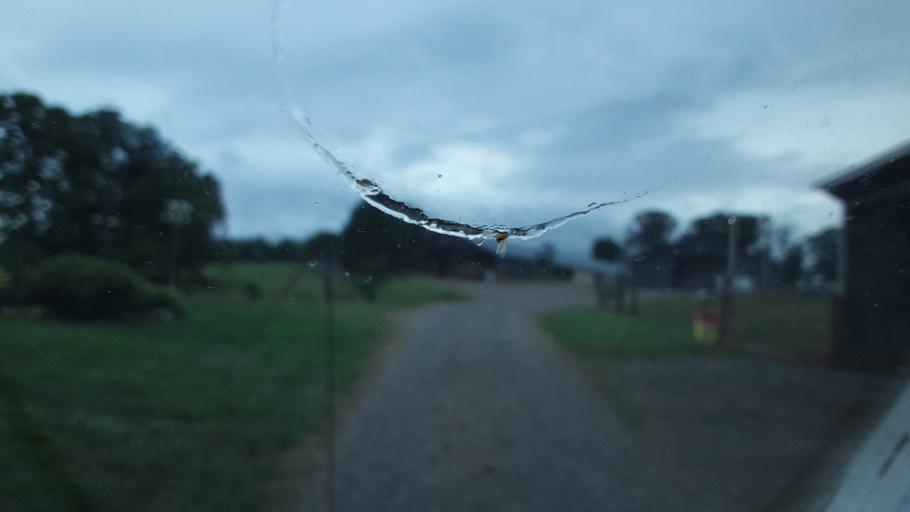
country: US
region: North Carolina
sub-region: Yadkin County
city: Jonesville
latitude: 36.1162
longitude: -80.8606
